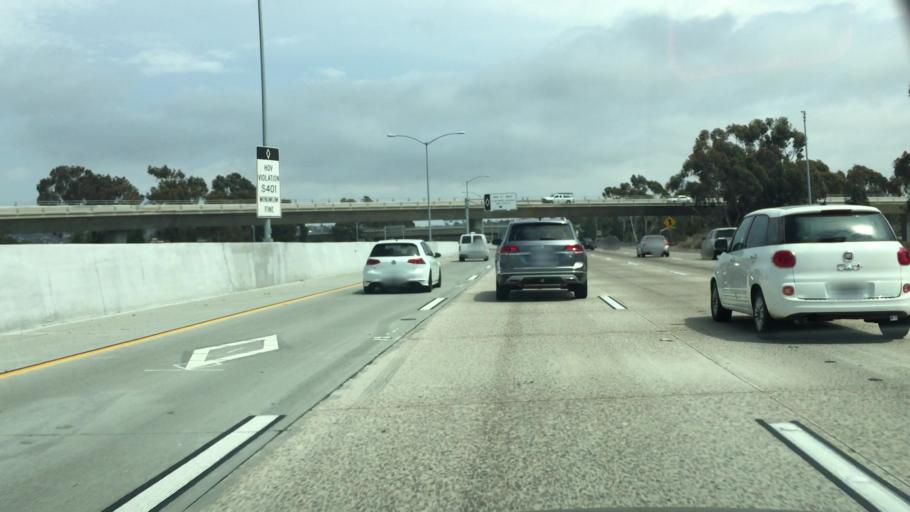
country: US
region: California
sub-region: San Diego County
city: Chula Vista
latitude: 32.6600
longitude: -117.0761
